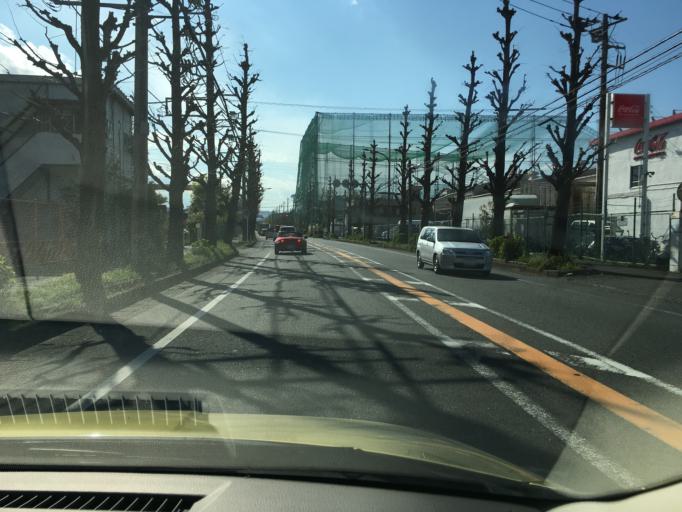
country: JP
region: Tokyo
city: Hachioji
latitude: 35.5760
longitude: 139.3565
